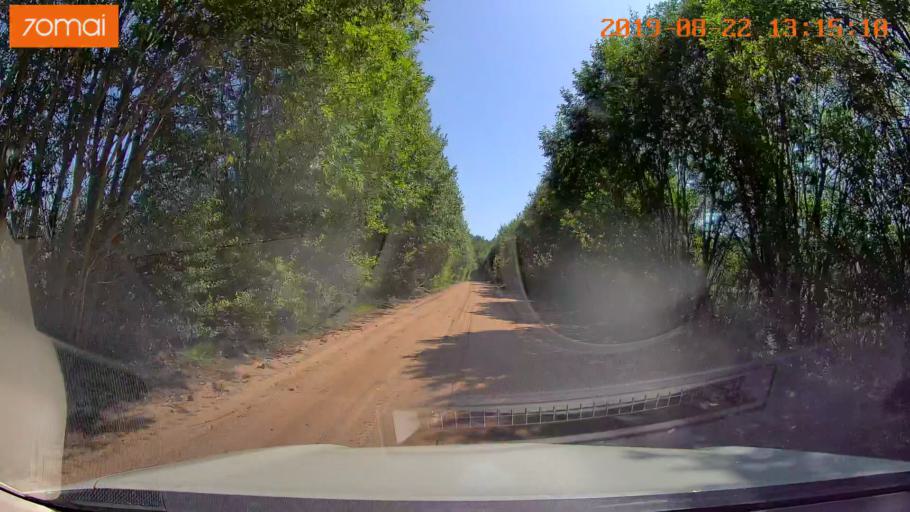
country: BY
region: Minsk
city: Prawdzinski
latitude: 53.2622
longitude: 27.8938
